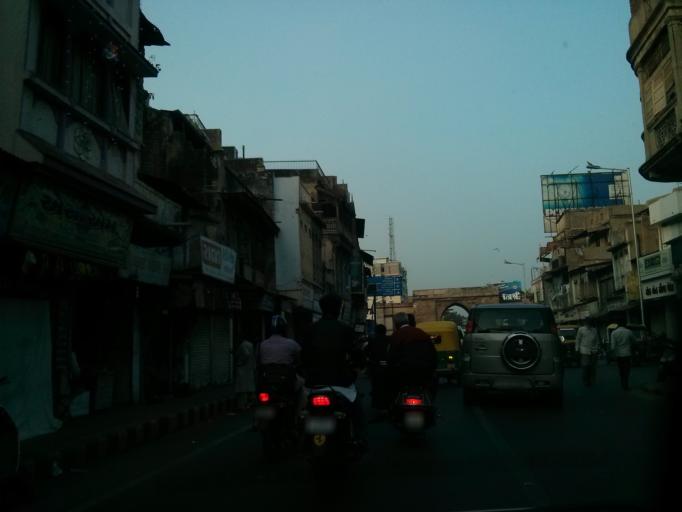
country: IN
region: Gujarat
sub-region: Ahmadabad
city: Ahmedabad
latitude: 23.0370
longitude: 72.5879
